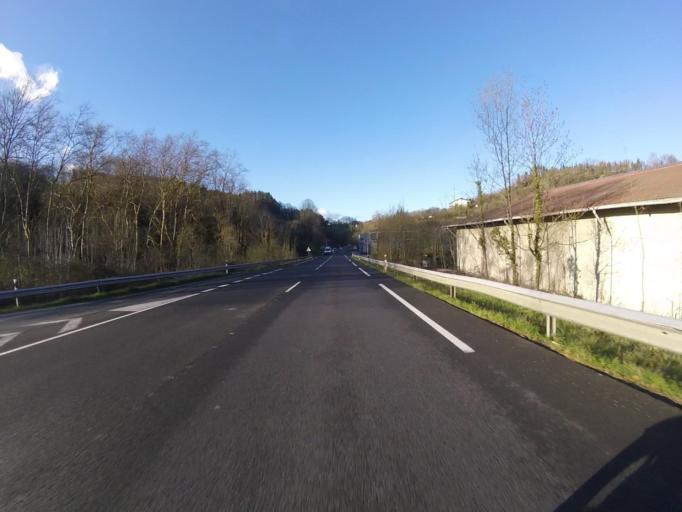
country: ES
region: Basque Country
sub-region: Provincia de Guipuzcoa
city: Errenteria
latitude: 43.2927
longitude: -1.8822
